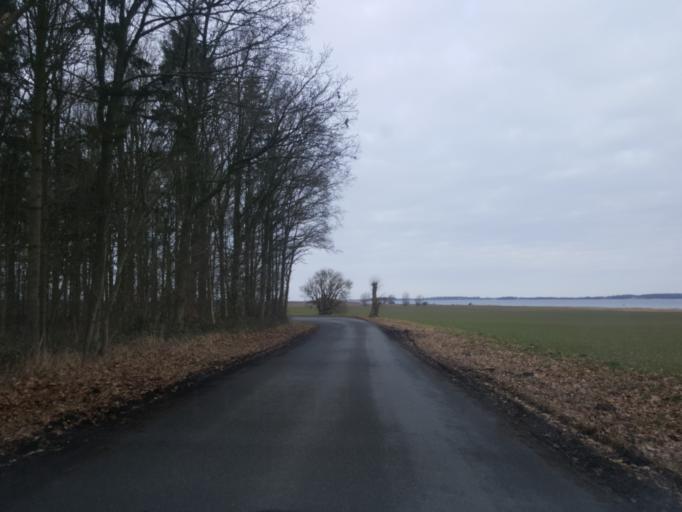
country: DK
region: Zealand
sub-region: Vordingborg Kommune
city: Neder Vindinge
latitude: 55.0412
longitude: 11.8118
